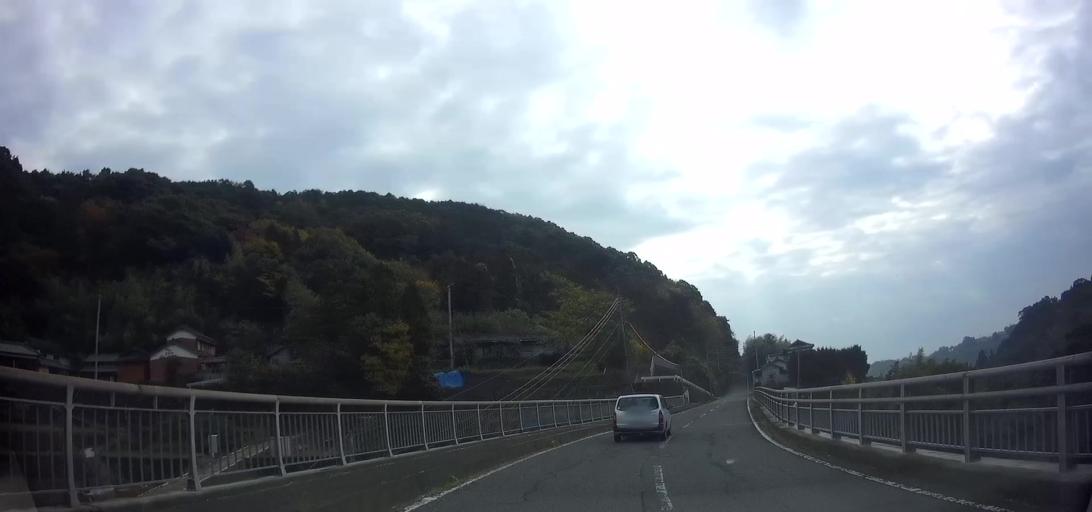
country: JP
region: Nagasaki
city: Shimabara
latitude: 32.6883
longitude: 130.2750
